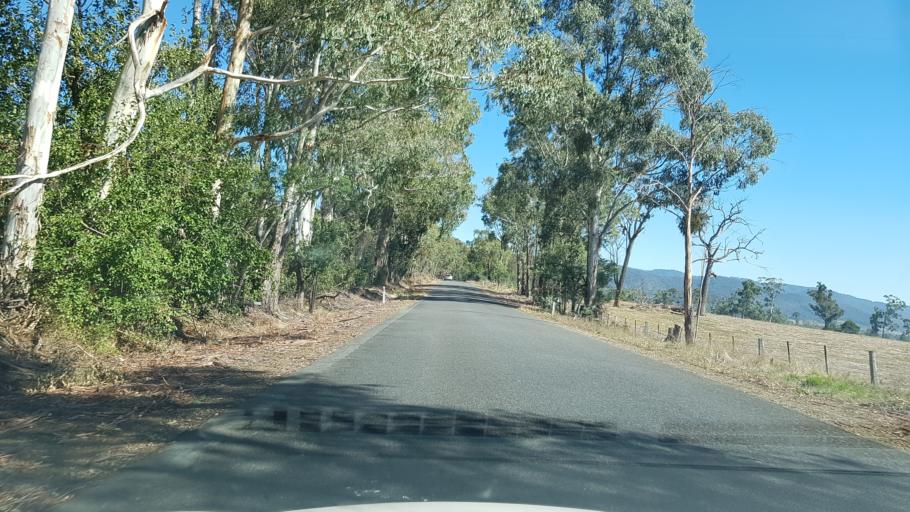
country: AU
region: Victoria
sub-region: Mansfield
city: Mansfield
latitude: -36.8151
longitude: 146.4539
